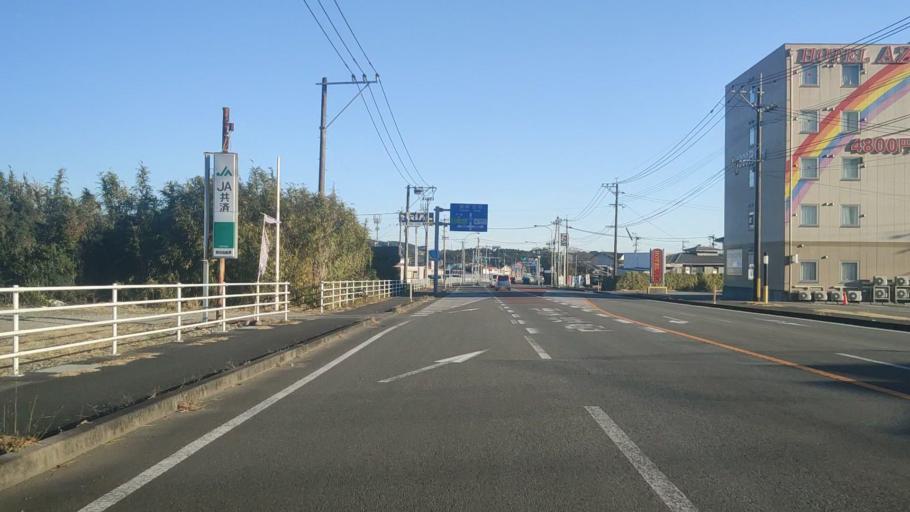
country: JP
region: Miyazaki
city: Takanabe
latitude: 32.2531
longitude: 131.5531
